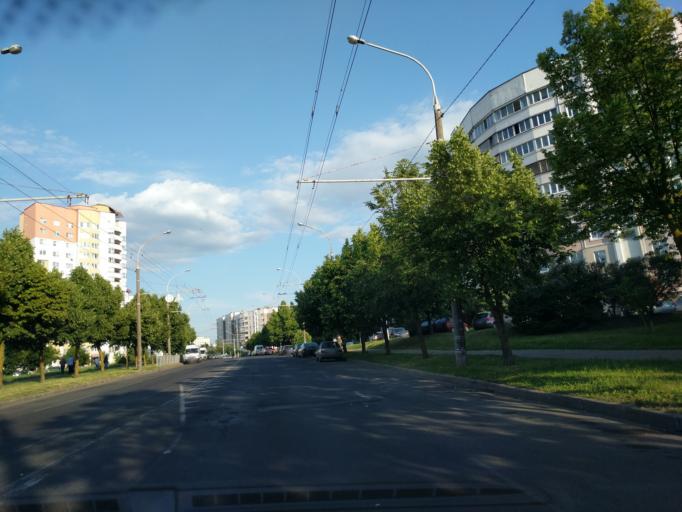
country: BY
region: Minsk
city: Malinovka
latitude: 53.8527
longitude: 27.4494
